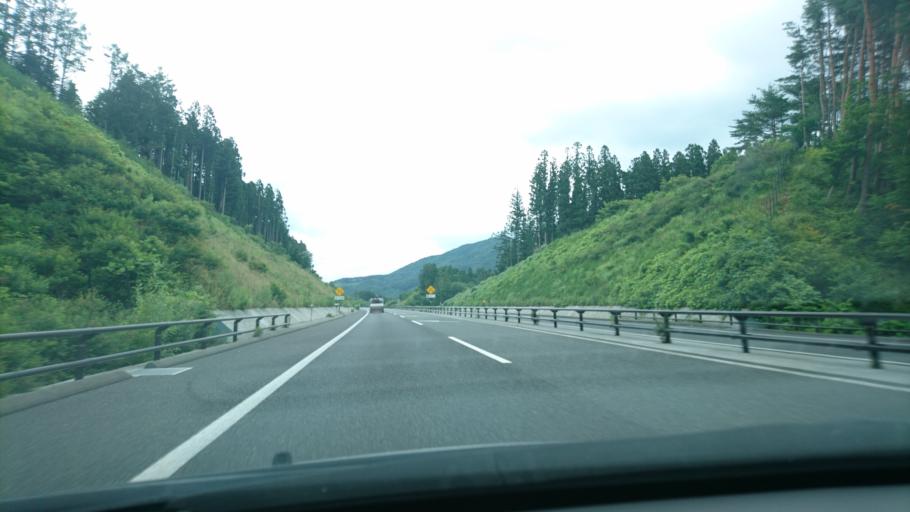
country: JP
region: Iwate
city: Ofunato
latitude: 39.0276
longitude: 141.6610
